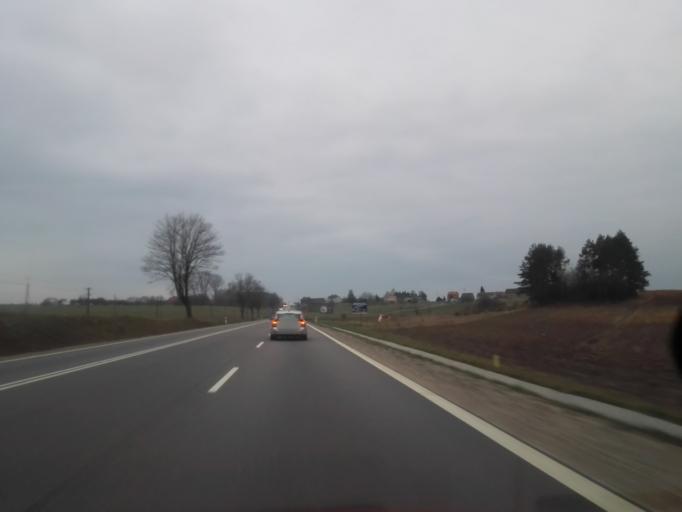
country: PL
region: Podlasie
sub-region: Powiat lomzynski
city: Piatnica
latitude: 53.2353
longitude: 22.1141
